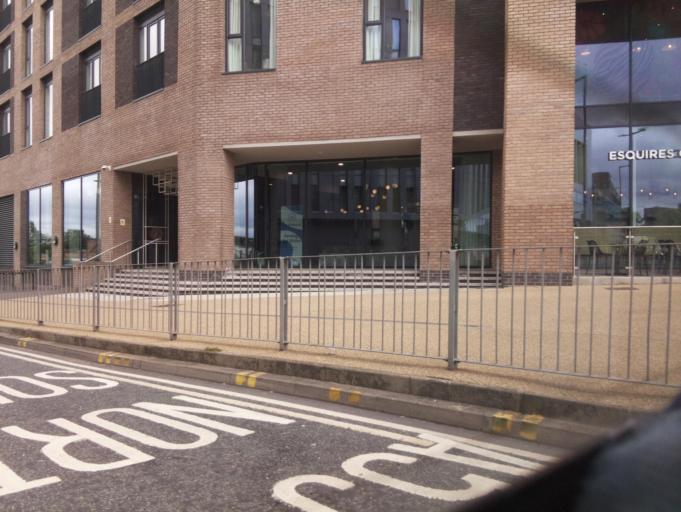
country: GB
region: England
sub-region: City of Leicester
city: Leicester
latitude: 52.6374
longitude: -1.1399
